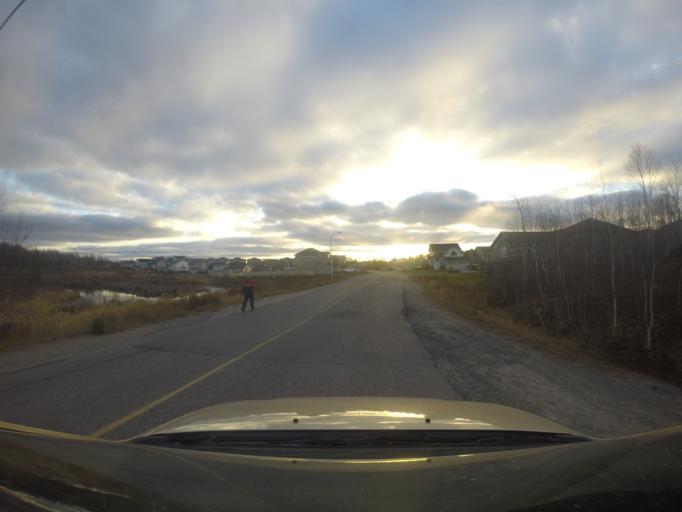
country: CA
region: Ontario
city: Greater Sudbury
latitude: 46.4857
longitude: -80.9337
